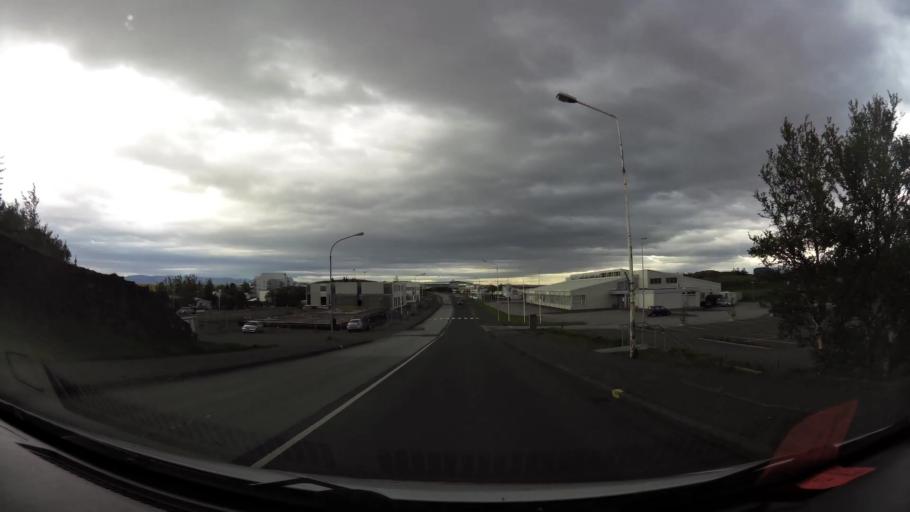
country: IS
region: West
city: Borgarnes
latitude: 64.5423
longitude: -21.9139
